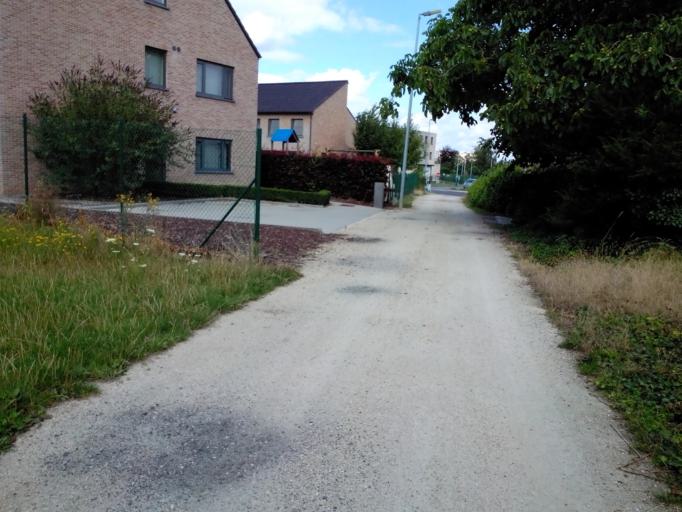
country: BE
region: Flanders
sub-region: Provincie Vlaams-Brabant
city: Leuven
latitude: 50.8710
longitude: 4.6838
